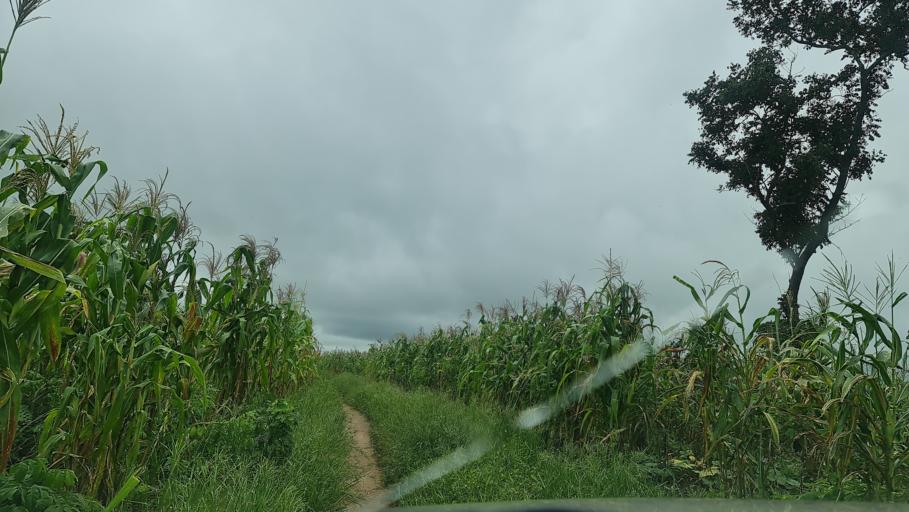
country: MW
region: Southern Region
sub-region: Nsanje District
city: Nsanje
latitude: -17.3435
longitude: 35.7337
